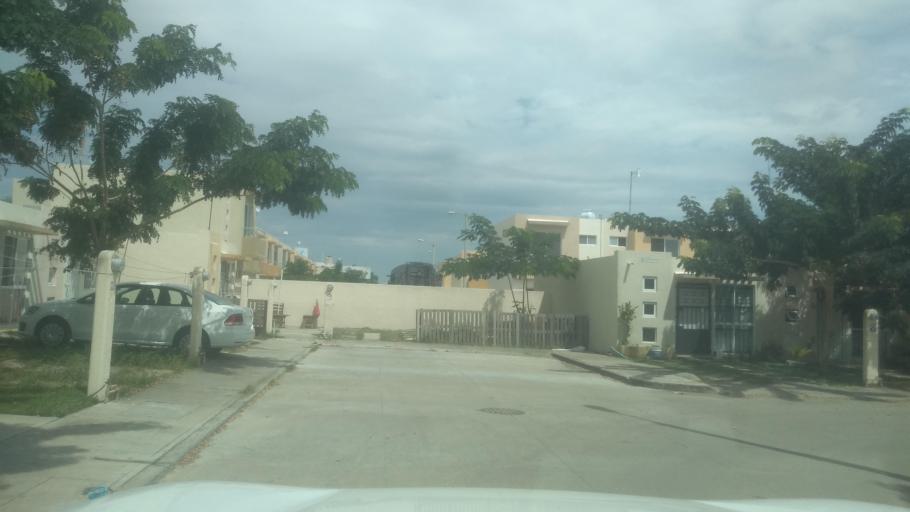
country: MX
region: Veracruz
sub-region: Medellin
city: Fraccionamiento Arboledas San Ramon
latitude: 19.1014
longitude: -96.1691
